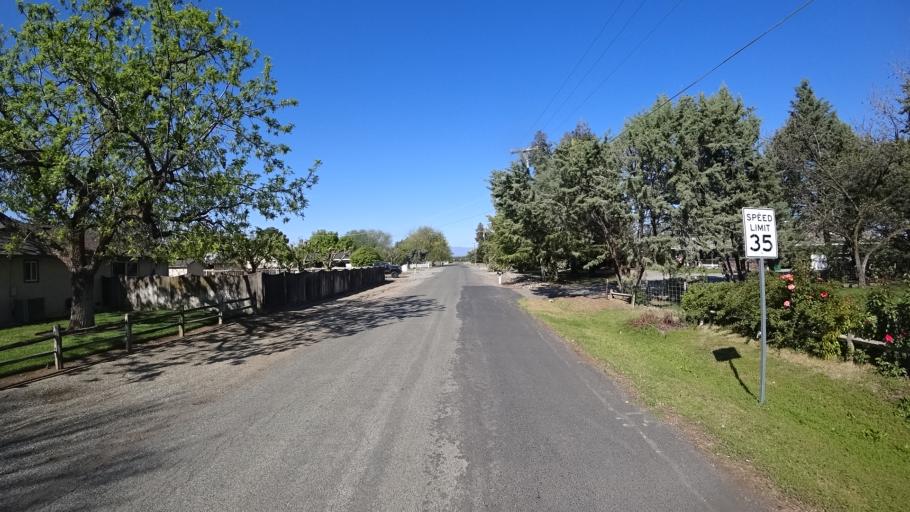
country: US
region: California
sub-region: Glenn County
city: Willows
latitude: 39.5334
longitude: -122.2079
